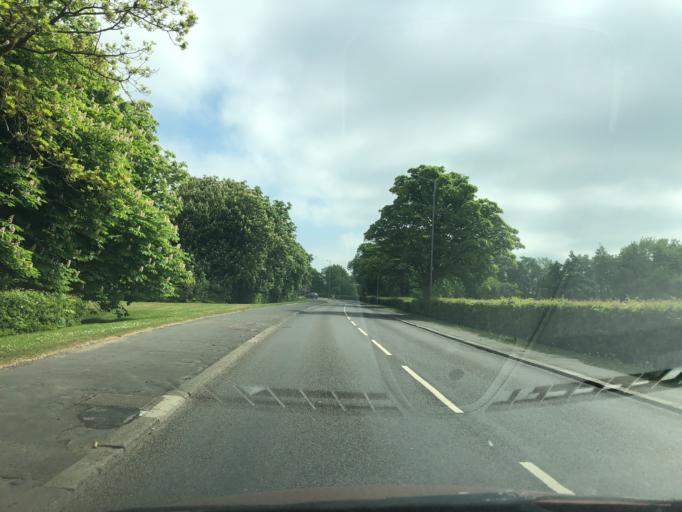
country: GB
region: England
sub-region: North Yorkshire
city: Catterick Garrison
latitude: 54.3813
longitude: -1.7251
